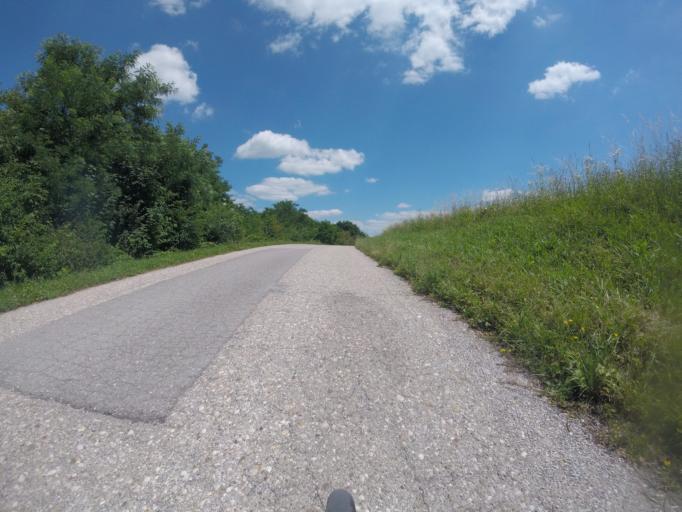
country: HR
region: Karlovacka
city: Ozalj
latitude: 45.6741
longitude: 15.4607
